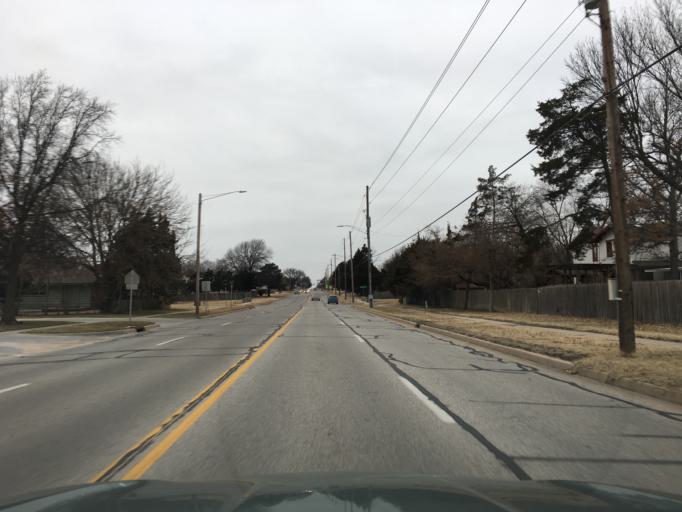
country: US
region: Kansas
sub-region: Sedgwick County
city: Bellaire
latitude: 37.7084
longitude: -97.2553
